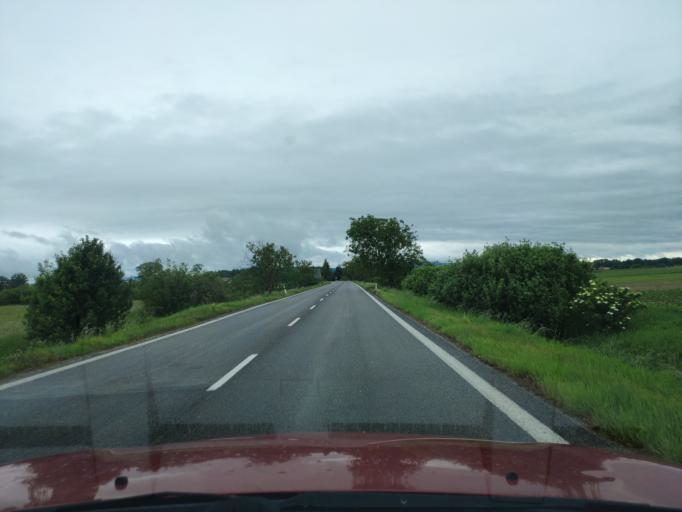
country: HU
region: Borsod-Abauj-Zemplen
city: Karcsa
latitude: 48.4343
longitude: 21.8746
